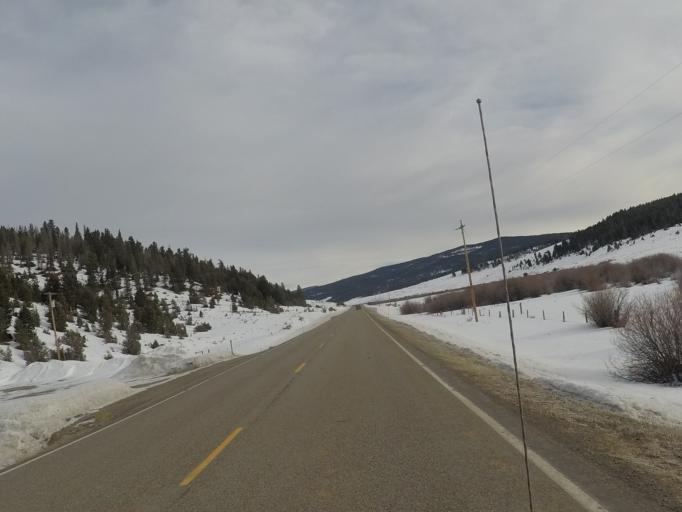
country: US
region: Montana
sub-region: Meagher County
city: White Sulphur Springs
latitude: 46.7077
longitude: -110.8620
